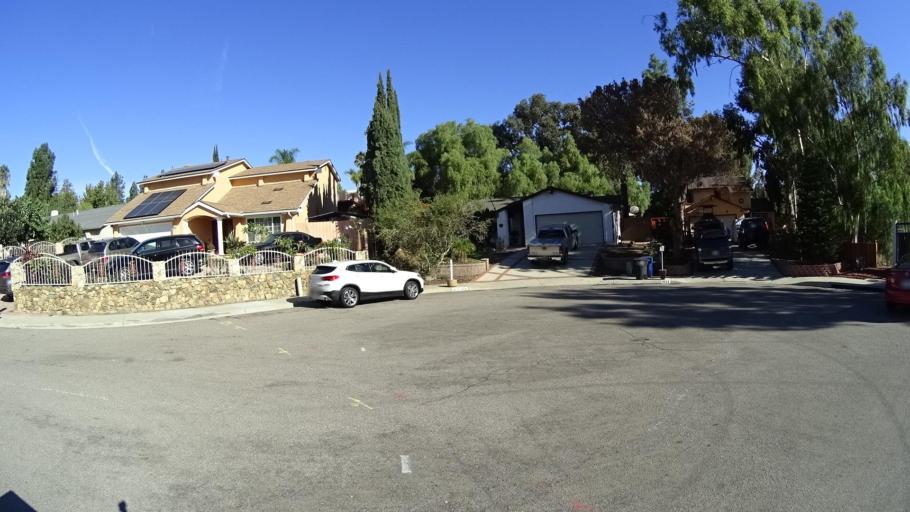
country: US
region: California
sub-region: San Diego County
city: La Presa
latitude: 32.7023
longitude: -116.9981
